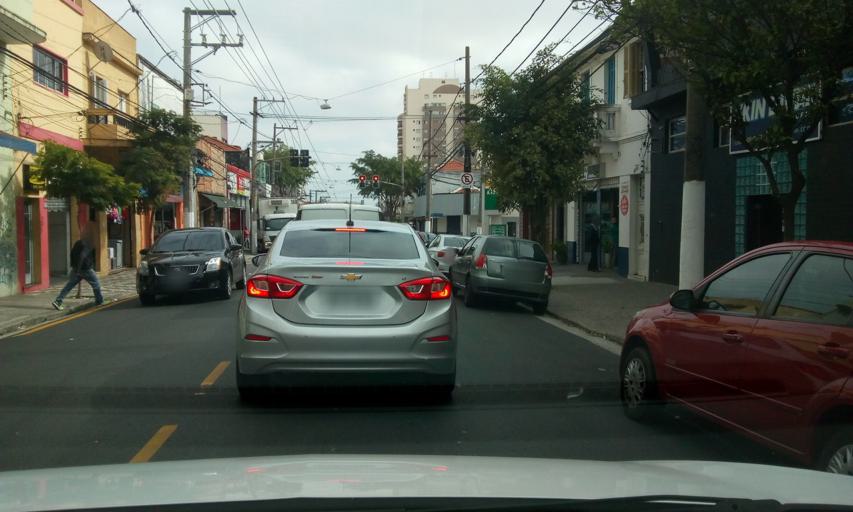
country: BR
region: Sao Paulo
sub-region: Sao Paulo
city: Sao Paulo
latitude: -23.5575
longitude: -46.5924
